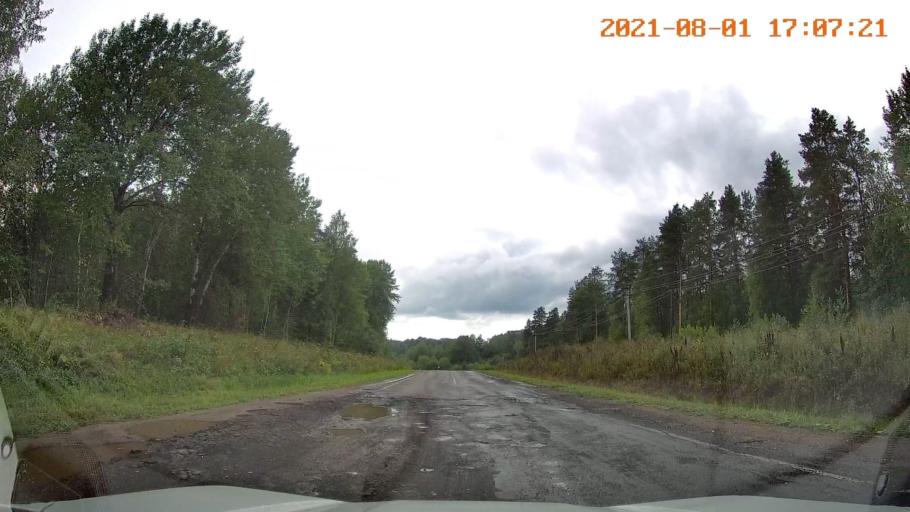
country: RU
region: Vologda
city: Vytegra
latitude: 61.0013
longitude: 36.3142
